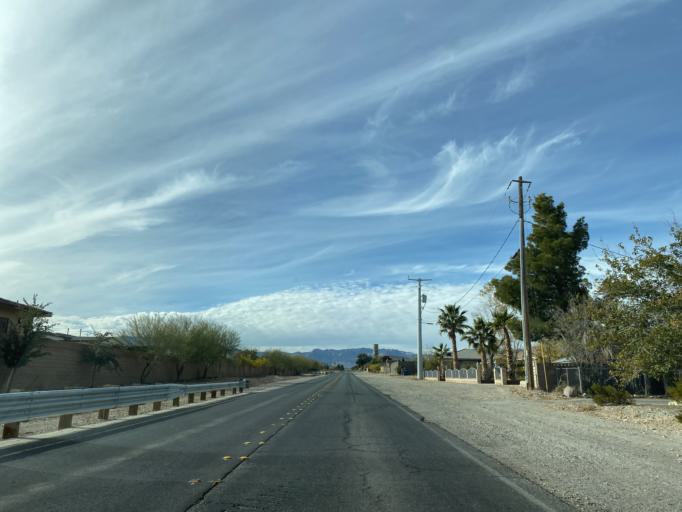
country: US
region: Nevada
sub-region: Clark County
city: Enterprise
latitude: 36.0337
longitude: -115.2632
